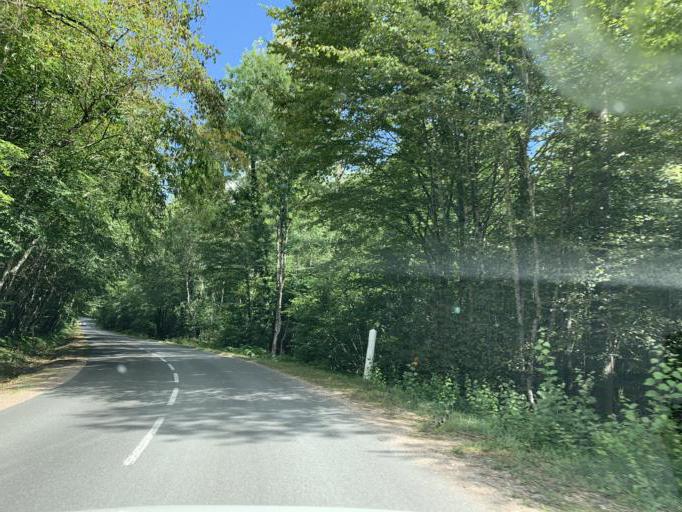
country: FR
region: Bourgogne
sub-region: Departement de la Nievre
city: Saint-Amand-en-Puisaye
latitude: 47.5821
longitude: 3.1592
